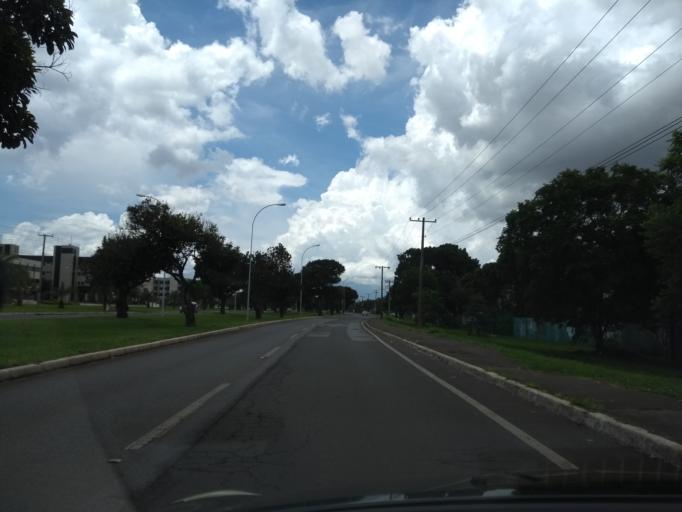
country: BR
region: Federal District
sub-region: Brasilia
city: Brasilia
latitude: -15.7877
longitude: -47.9319
